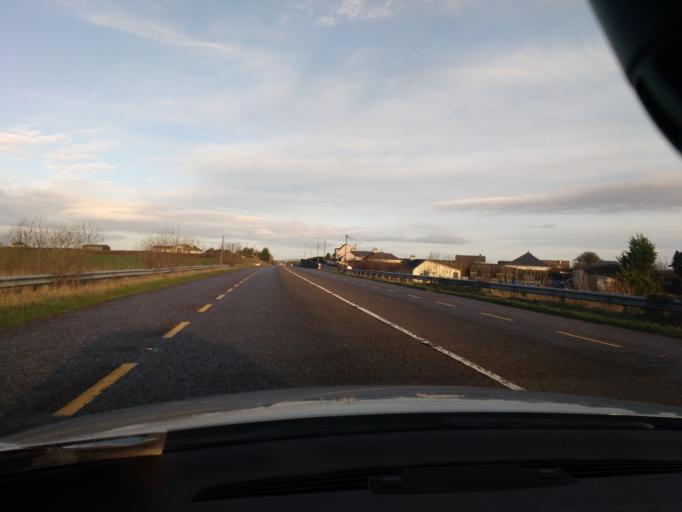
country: IE
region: Munster
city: Thurles
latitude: 52.6587
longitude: -7.7034
